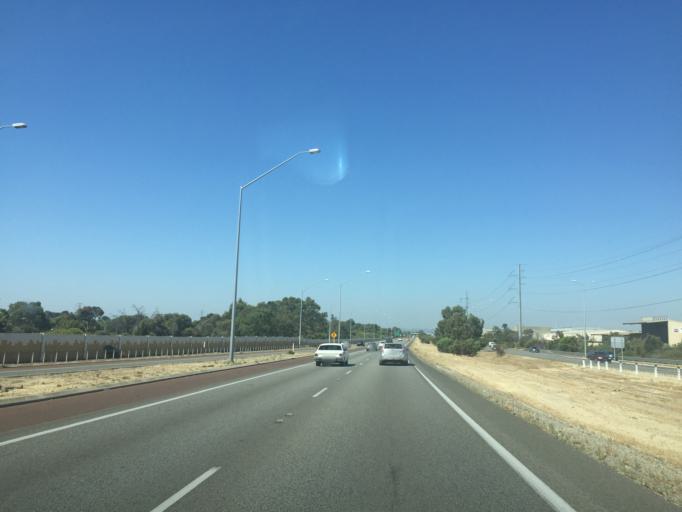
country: AU
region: Western Australia
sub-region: Canning
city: Willetton
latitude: -32.0665
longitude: 115.8928
